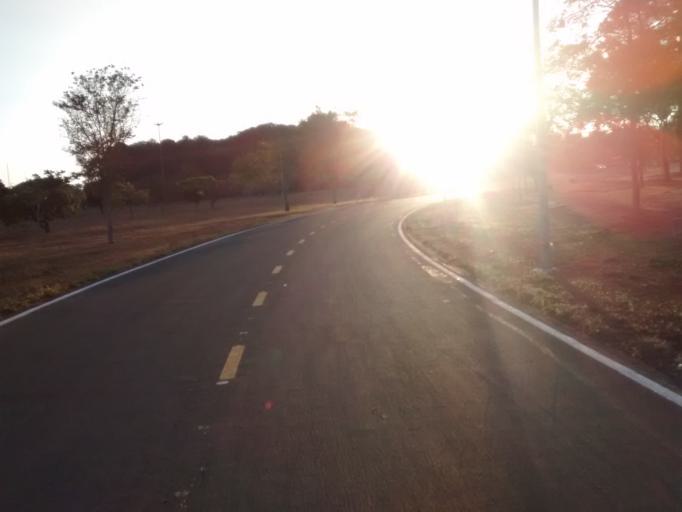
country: BR
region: Federal District
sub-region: Brasilia
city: Brasilia
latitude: -15.8066
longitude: -47.9194
